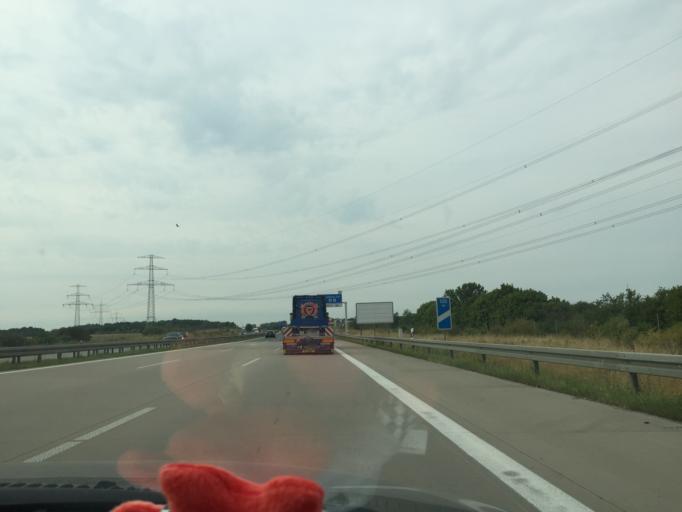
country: DE
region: Brandenburg
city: Neuenhagen
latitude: 52.5390
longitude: 13.6980
